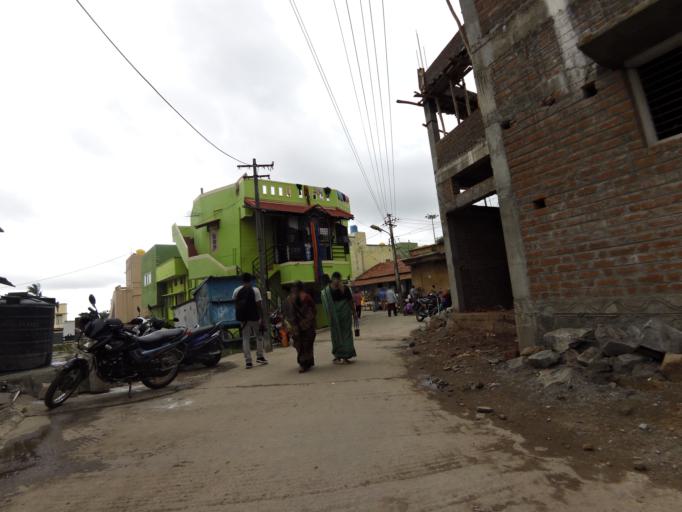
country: IN
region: Karnataka
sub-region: Mysore
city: Mysore
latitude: 12.2733
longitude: 76.6714
